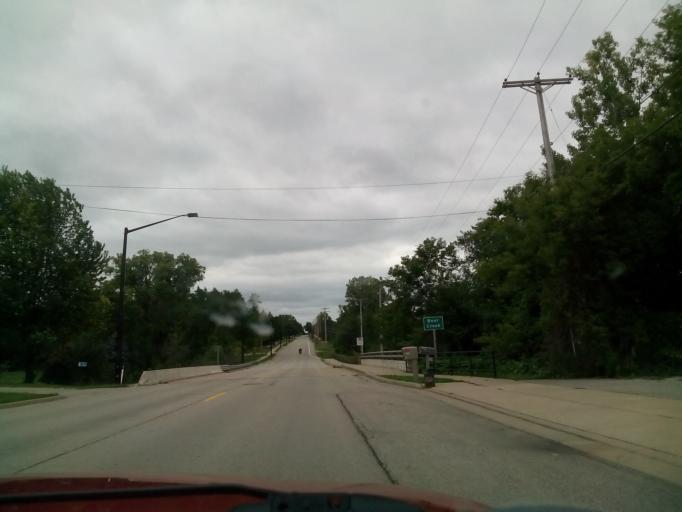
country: US
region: Wisconsin
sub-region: Outagamie County
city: Hortonville
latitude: 44.3717
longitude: -88.5846
